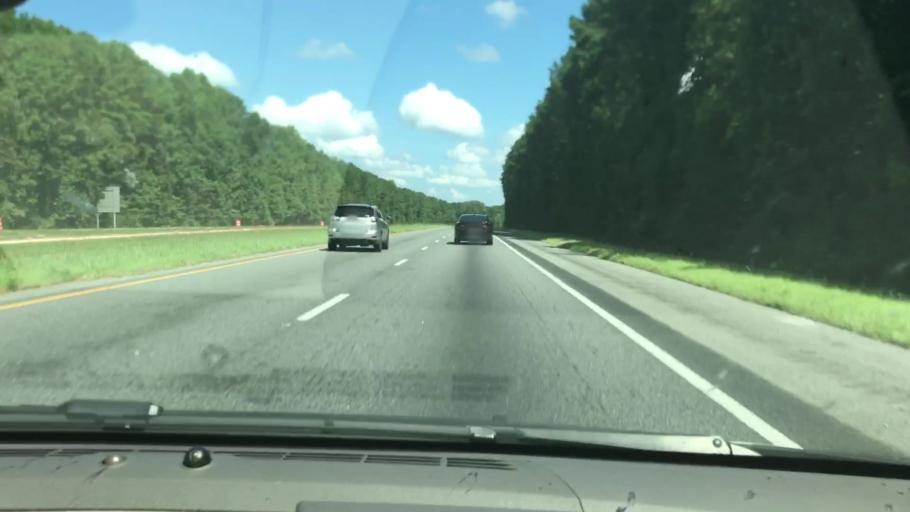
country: US
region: Georgia
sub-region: Harris County
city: Hamilton
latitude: 32.7647
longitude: -85.0184
